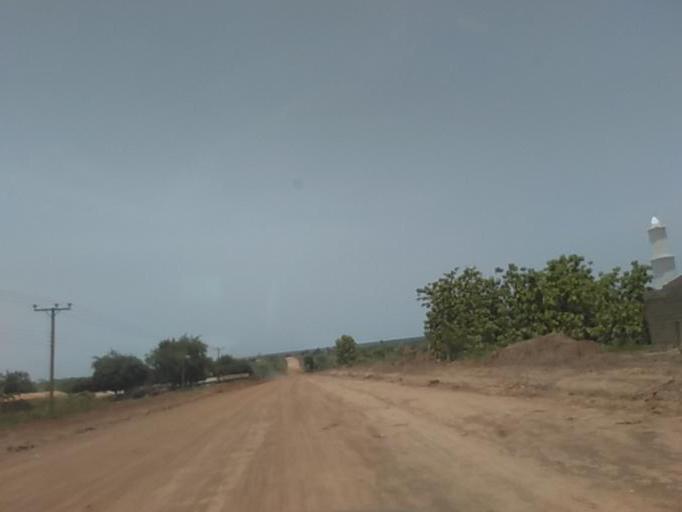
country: GH
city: Kpandae
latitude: 8.6321
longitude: 0.2240
